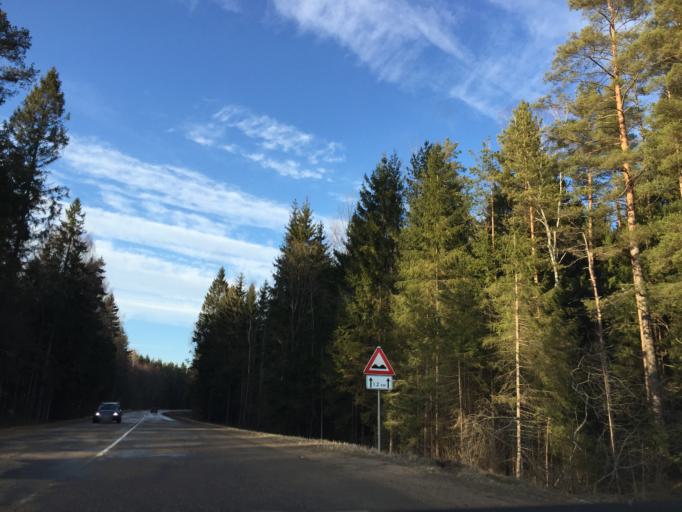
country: LV
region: Kekava
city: Balozi
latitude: 56.7579
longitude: 24.1098
